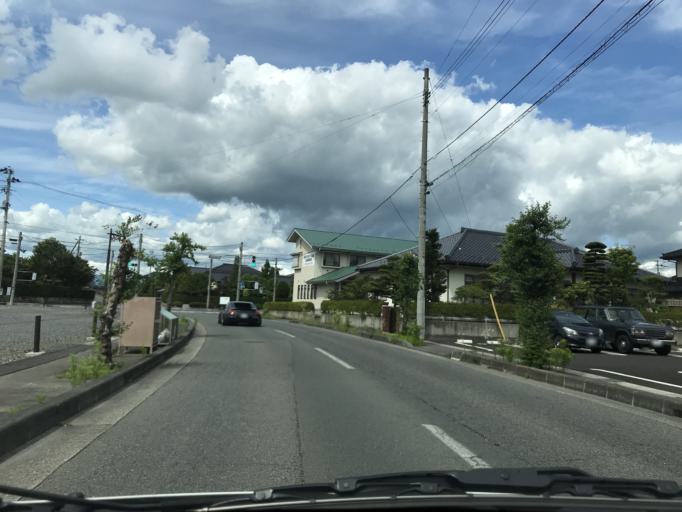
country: JP
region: Iwate
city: Tono
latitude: 39.3291
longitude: 141.5367
